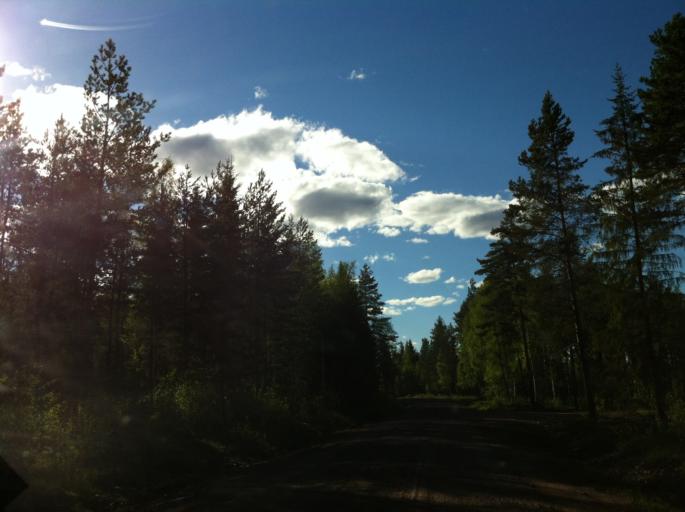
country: SE
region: Dalarna
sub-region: Leksand Municipality
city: Siljansnas
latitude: 60.7825
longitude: 14.8227
